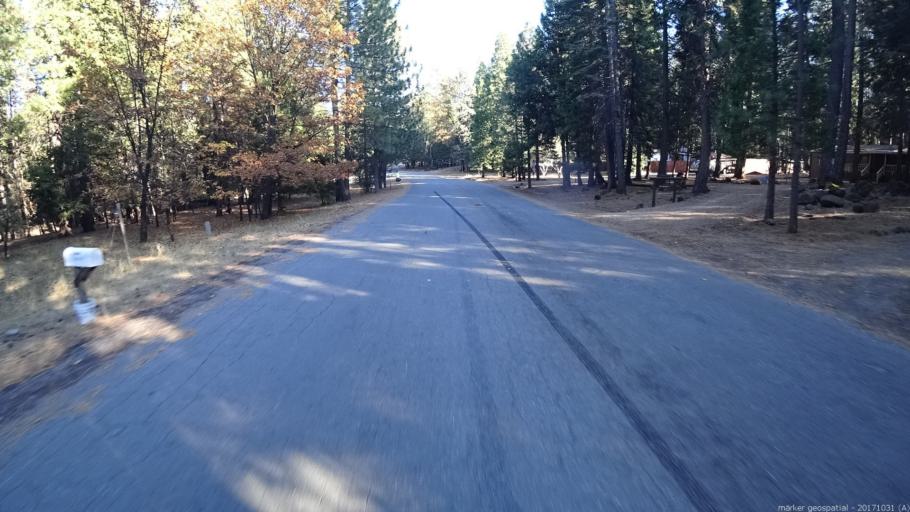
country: US
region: California
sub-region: Shasta County
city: Shingletown
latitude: 40.5001
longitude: -121.9071
